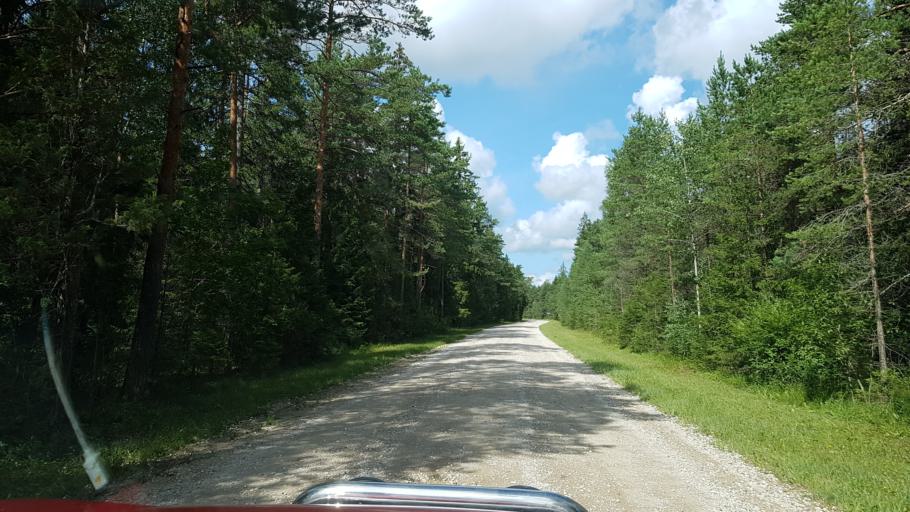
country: EE
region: Raplamaa
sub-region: Rapla vald
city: Rapla
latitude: 58.9597
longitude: 24.6470
